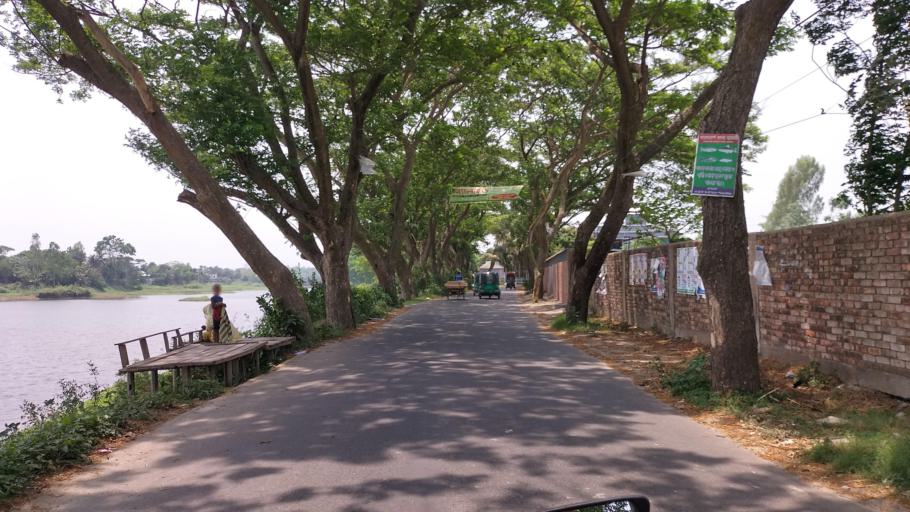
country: BD
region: Dhaka
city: Azimpur
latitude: 23.7407
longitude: 90.2488
